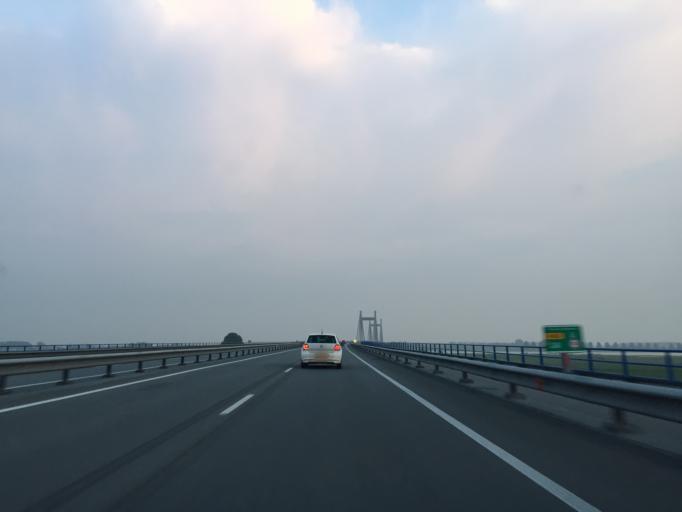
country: NL
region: Gelderland
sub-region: Gemeente Buren
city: Lienden
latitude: 51.8983
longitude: 5.4967
